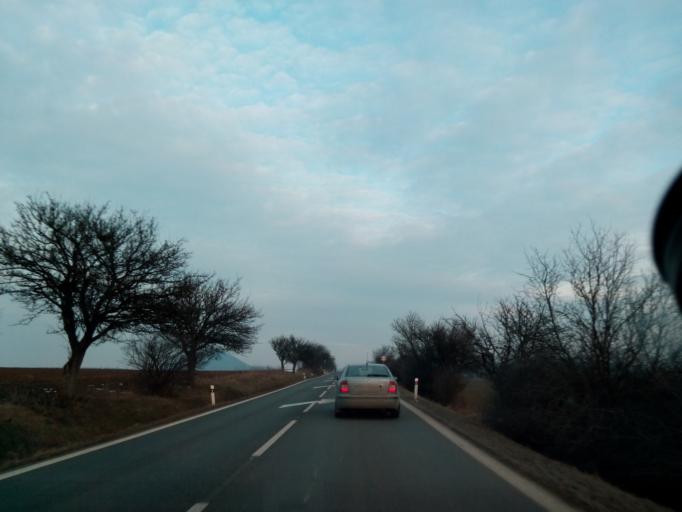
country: SK
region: Presovsky
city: Sabinov
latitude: 49.0673
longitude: 21.1455
